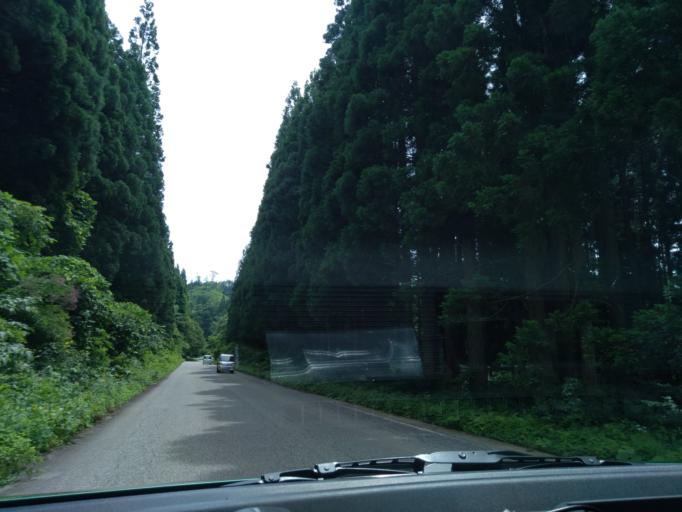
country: JP
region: Akita
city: Kakunodatemachi
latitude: 39.5707
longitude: 140.6347
